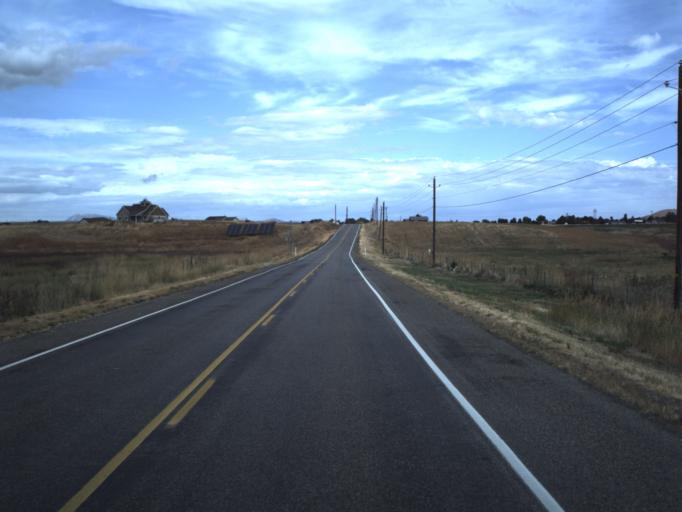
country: US
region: Utah
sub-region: Cache County
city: Benson
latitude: 41.8454
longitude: -112.0022
